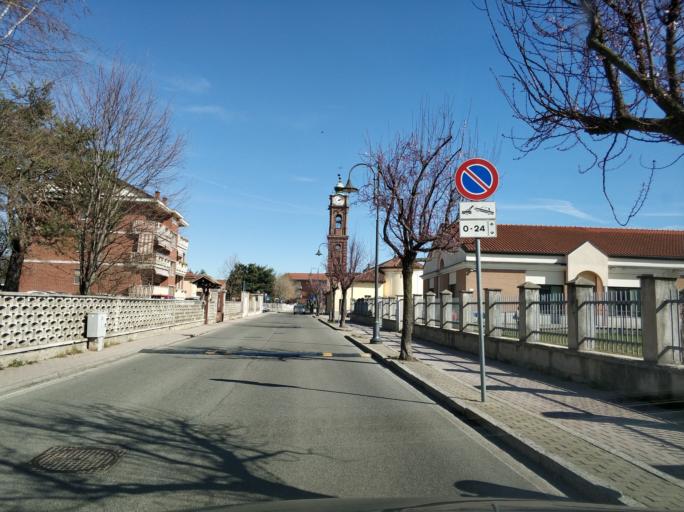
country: IT
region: Piedmont
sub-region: Provincia di Torino
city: Leini
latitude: 45.1868
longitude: 7.7162
